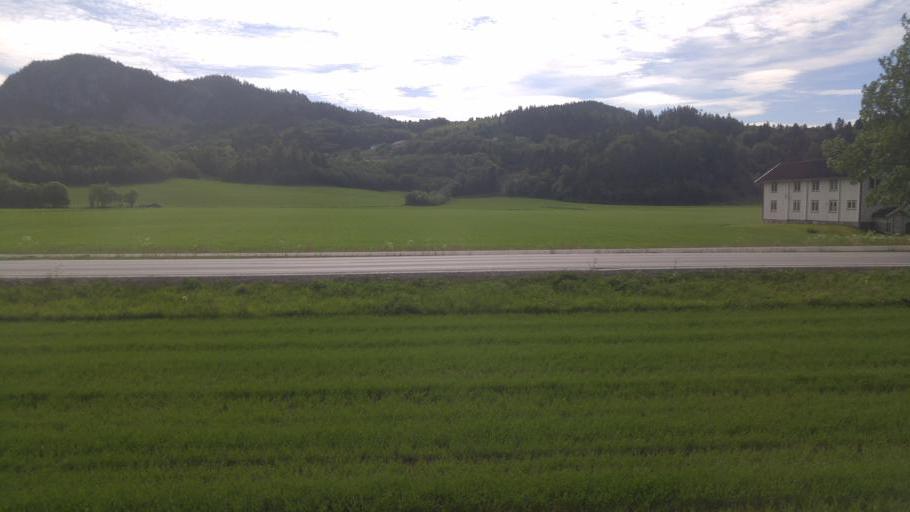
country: NO
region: Sor-Trondelag
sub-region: Melhus
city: Lundamo
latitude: 63.1457
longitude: 10.2649
